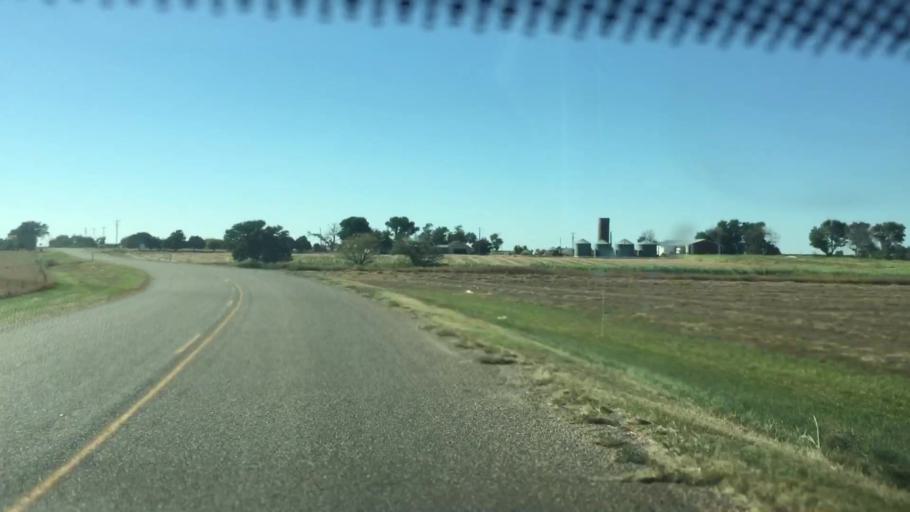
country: US
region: Colorado
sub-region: Prowers County
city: Lamar
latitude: 38.1176
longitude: -102.6097
